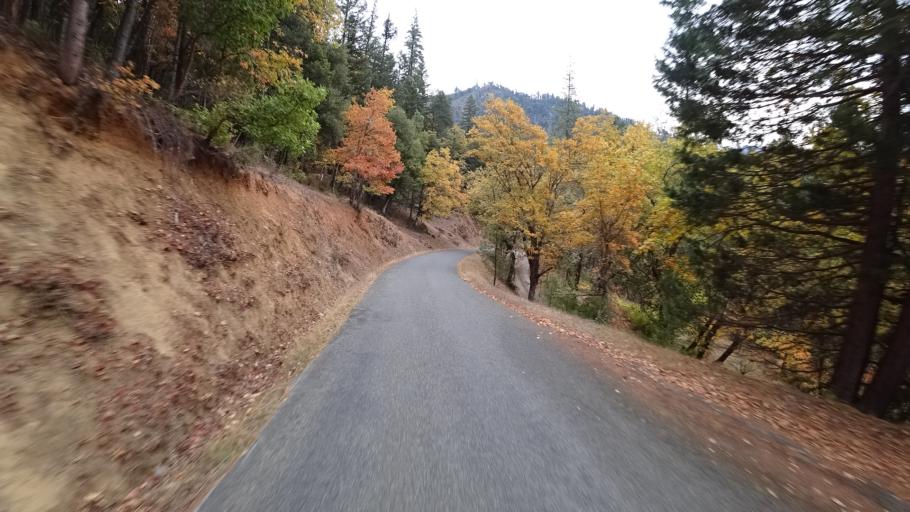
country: US
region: California
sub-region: Siskiyou County
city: Happy Camp
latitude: 41.7504
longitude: -123.3613
